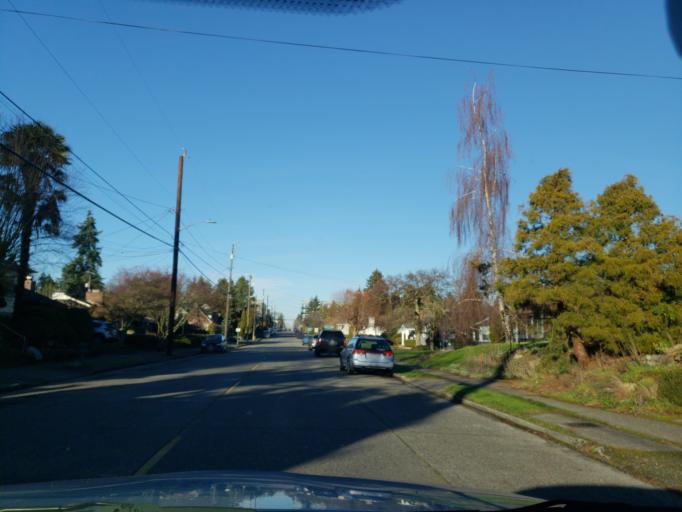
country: US
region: Washington
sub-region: King County
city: Lake Forest Park
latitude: 47.6875
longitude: -122.3068
